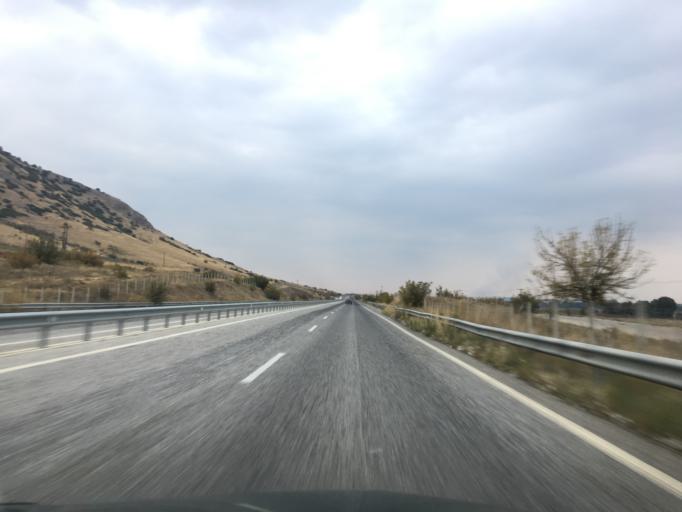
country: GR
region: Thessaly
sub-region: Trikala
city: Zarkos
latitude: 39.5967
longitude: 22.1896
